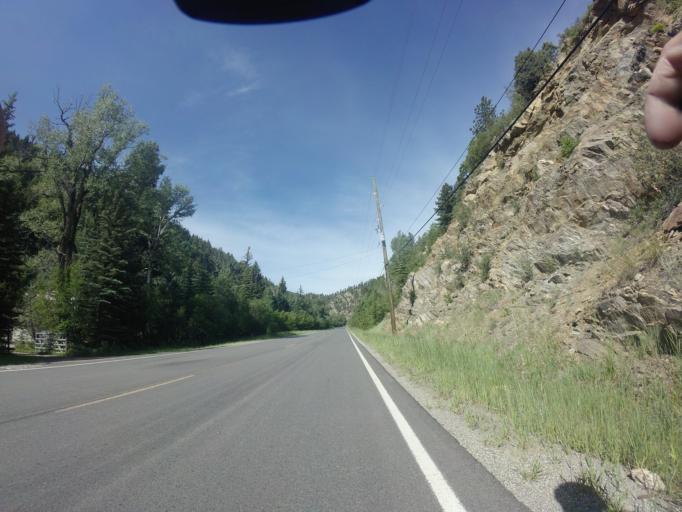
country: US
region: Colorado
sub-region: Clear Creek County
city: Idaho Springs
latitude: 39.7230
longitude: -105.5639
